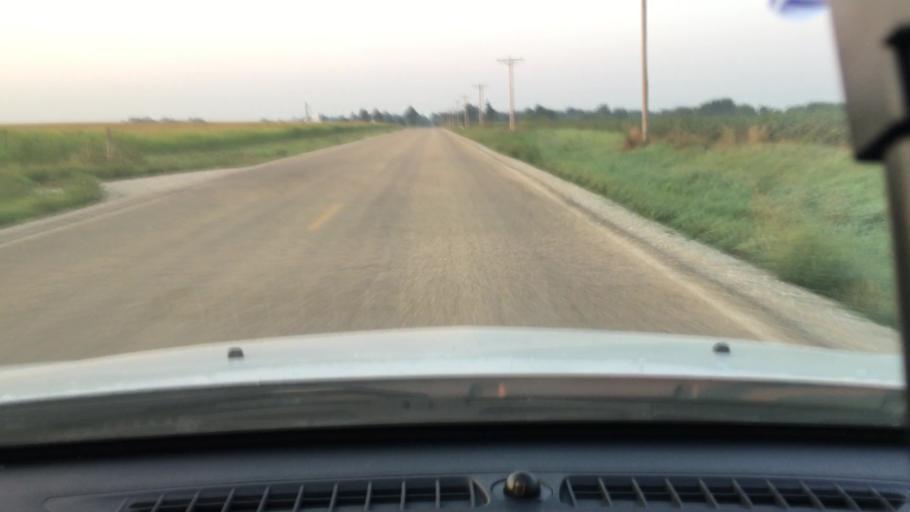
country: US
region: Illinois
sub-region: DeKalb County
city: Waterman
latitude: 41.7870
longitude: -88.7739
